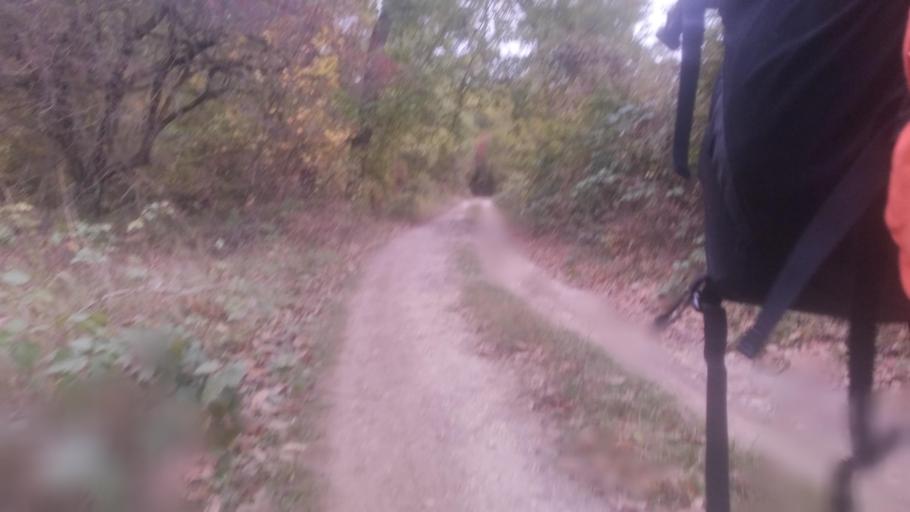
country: HU
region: Pest
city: Telki
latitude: 47.5344
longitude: 18.8664
